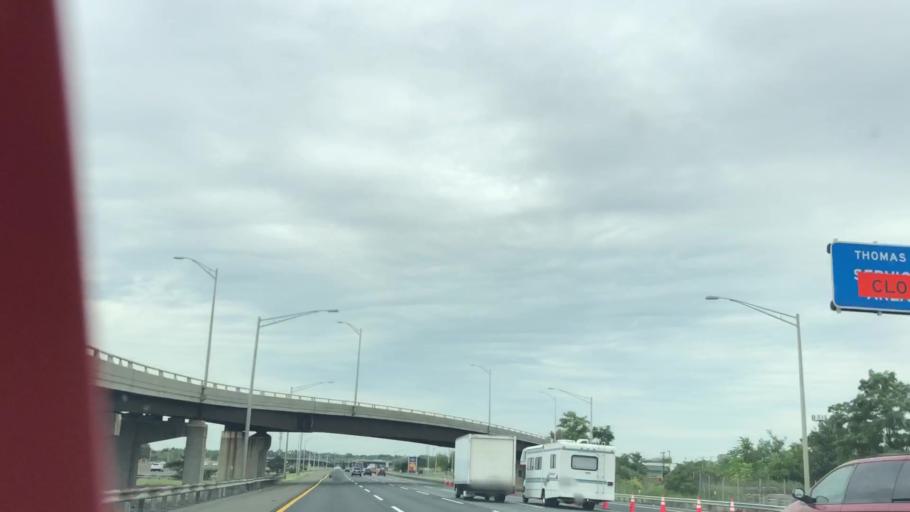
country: US
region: New Jersey
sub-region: Middlesex County
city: Port Reading
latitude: 40.5627
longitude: -74.2622
